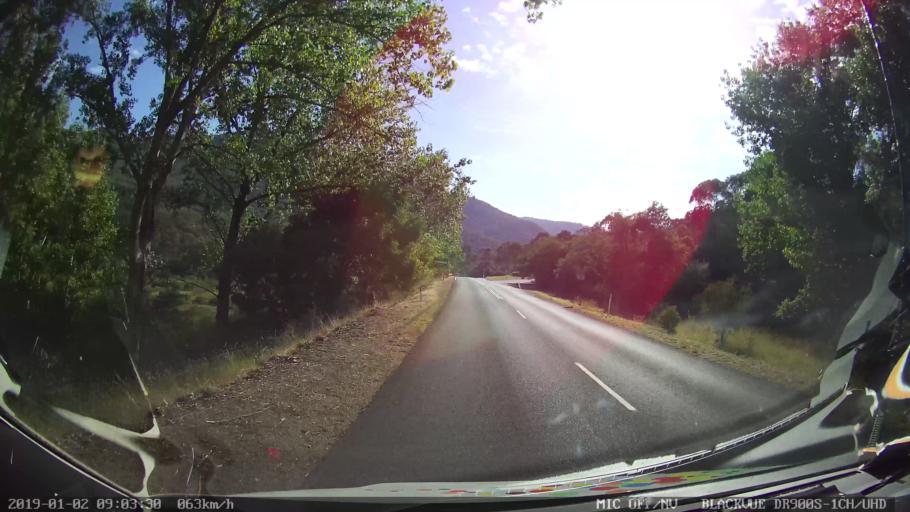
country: AU
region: New South Wales
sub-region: Tumut Shire
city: Tumut
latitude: -35.5686
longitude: 148.3241
